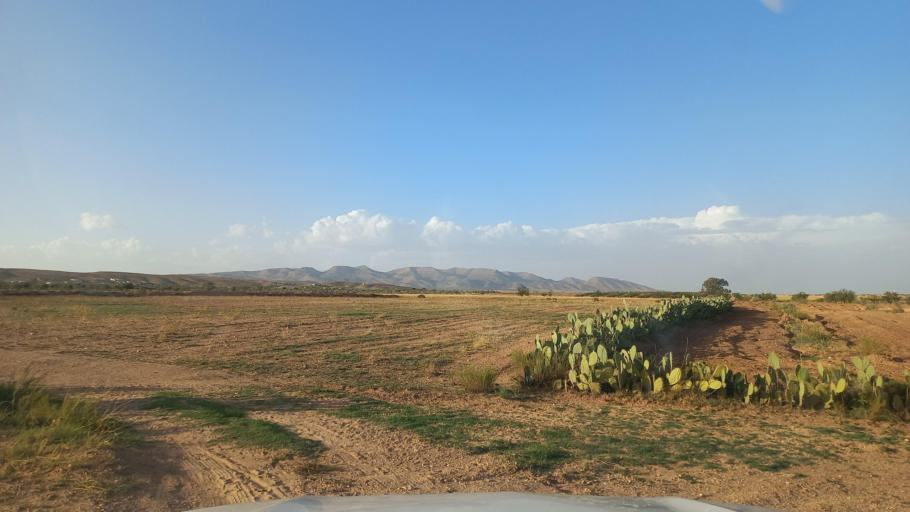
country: TN
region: Al Qasrayn
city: Sbiba
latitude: 35.3645
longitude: 9.0212
